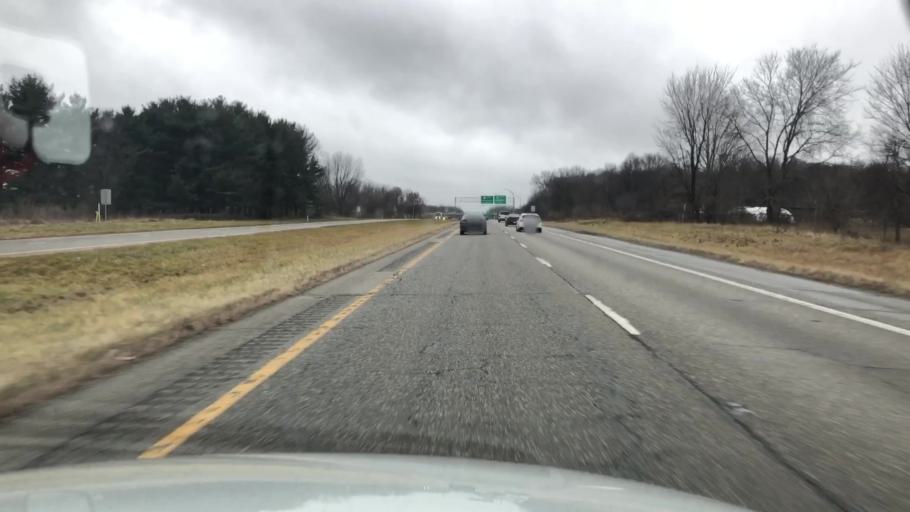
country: US
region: Indiana
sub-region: Marshall County
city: Plymouth
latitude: 41.3451
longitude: -86.2663
